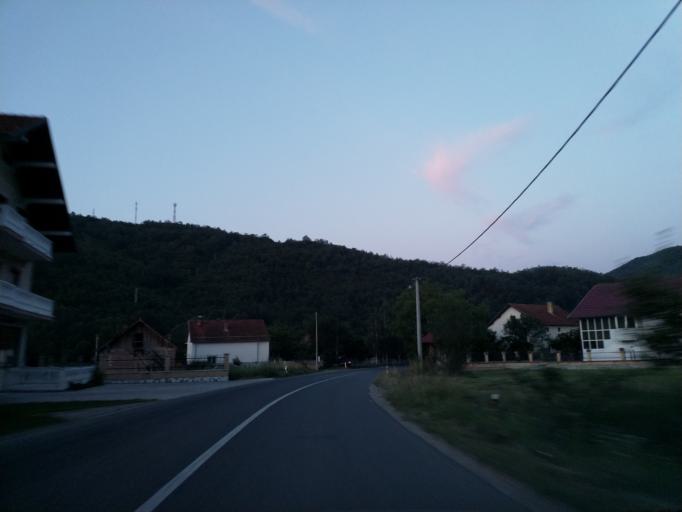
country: RS
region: Central Serbia
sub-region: Rasinski Okrug
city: Aleksandrovac
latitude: 43.3468
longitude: 21.0871
